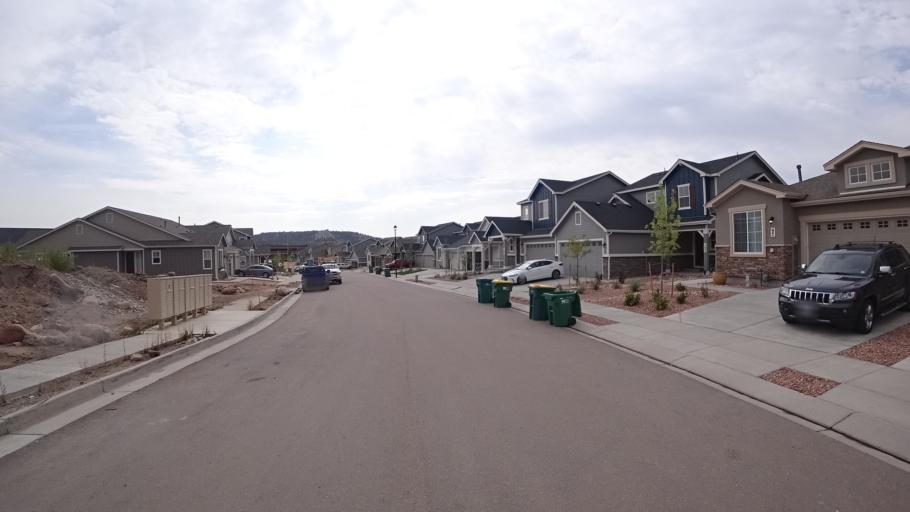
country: US
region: Colorado
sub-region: El Paso County
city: Colorado Springs
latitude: 38.9163
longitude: -104.8262
